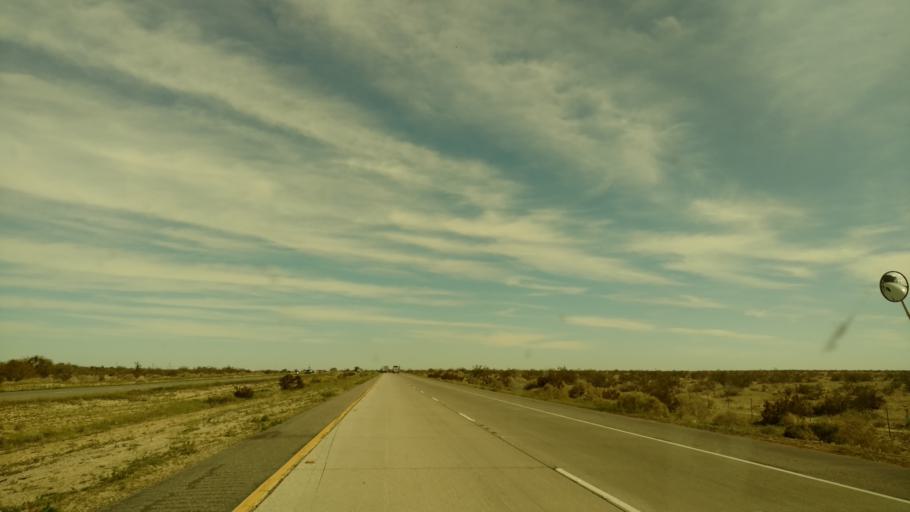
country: US
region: California
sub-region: Imperial County
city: Westmorland
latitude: 33.0938
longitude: -115.7789
